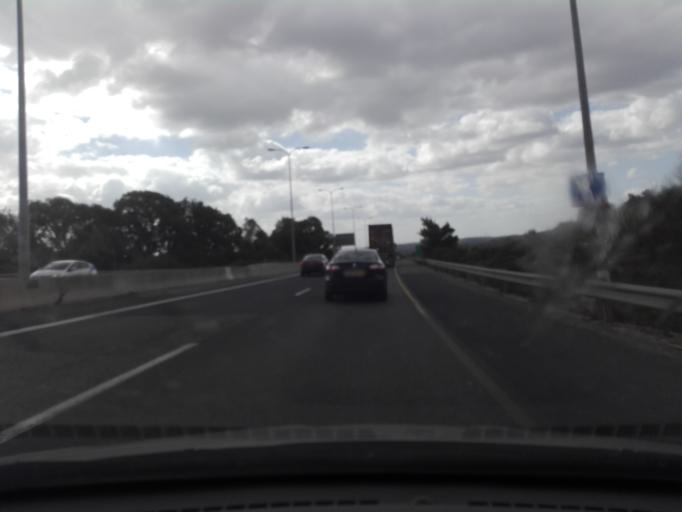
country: IL
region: Haifa
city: Daliyat el Karmil
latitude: 32.6277
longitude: 35.0619
